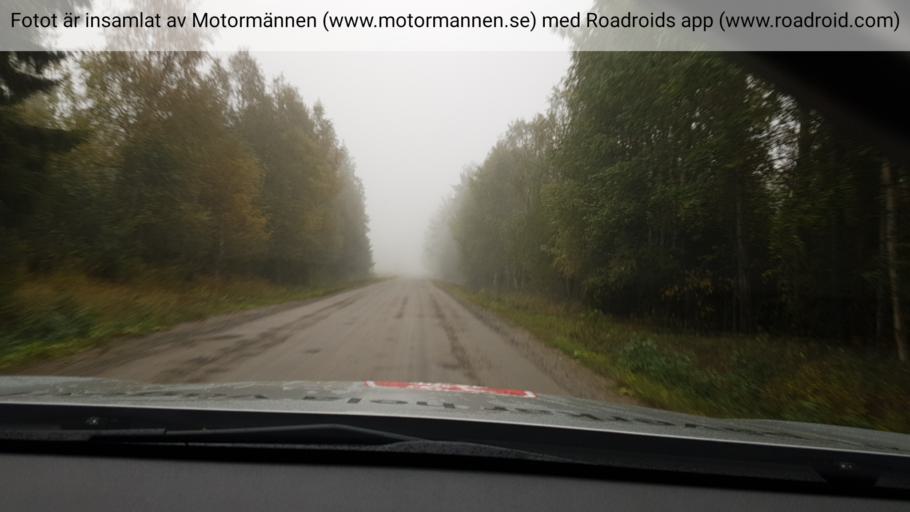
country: SE
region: Vaesterbotten
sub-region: Vannas Kommun
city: Vannasby
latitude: 64.0879
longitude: 20.0320
